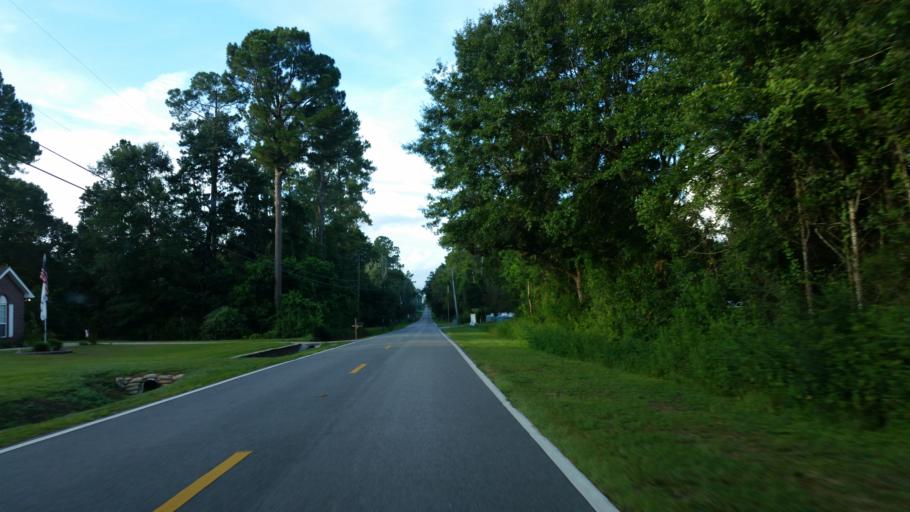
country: US
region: Florida
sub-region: Escambia County
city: Ensley
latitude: 30.5258
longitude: -87.3303
